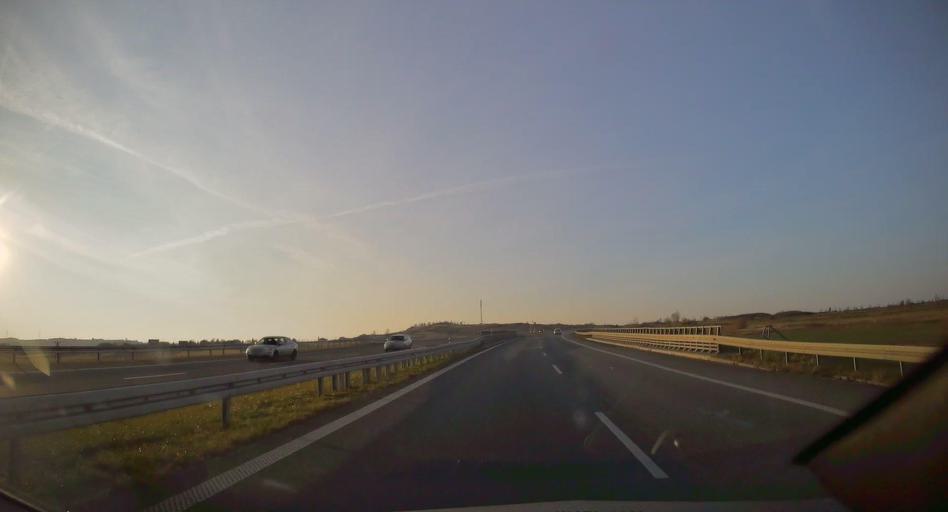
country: PL
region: Silesian Voivodeship
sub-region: Powiat bedzinski
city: Mierzecice
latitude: 50.4256
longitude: 19.1637
